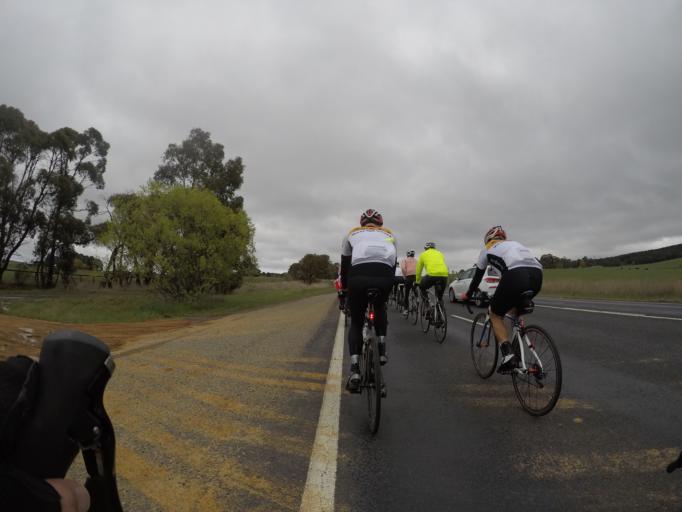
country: AU
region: New South Wales
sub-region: Lithgow
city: Portland
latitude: -33.4332
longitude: 149.9010
